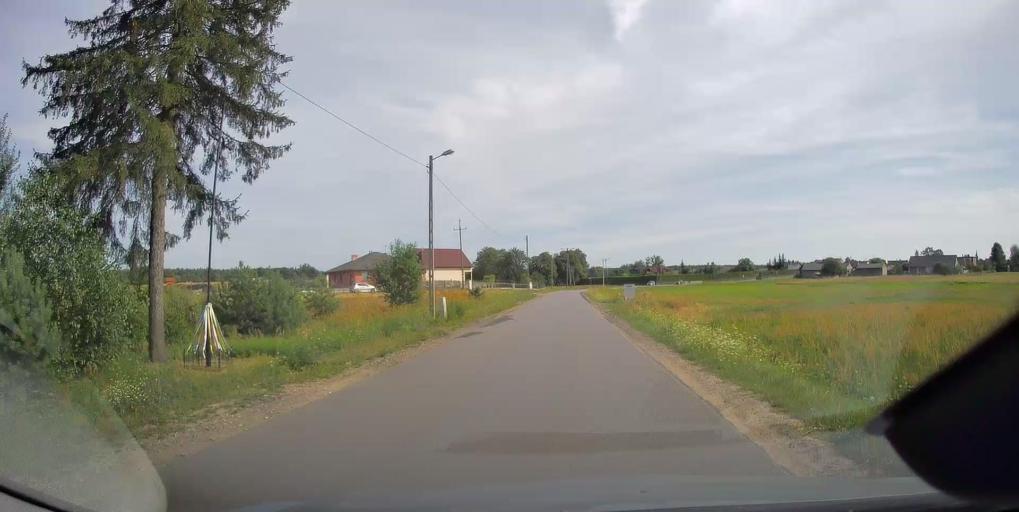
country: PL
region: Lodz Voivodeship
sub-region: Powiat tomaszowski
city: Tomaszow Mazowiecki
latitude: 51.4582
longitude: 20.0350
